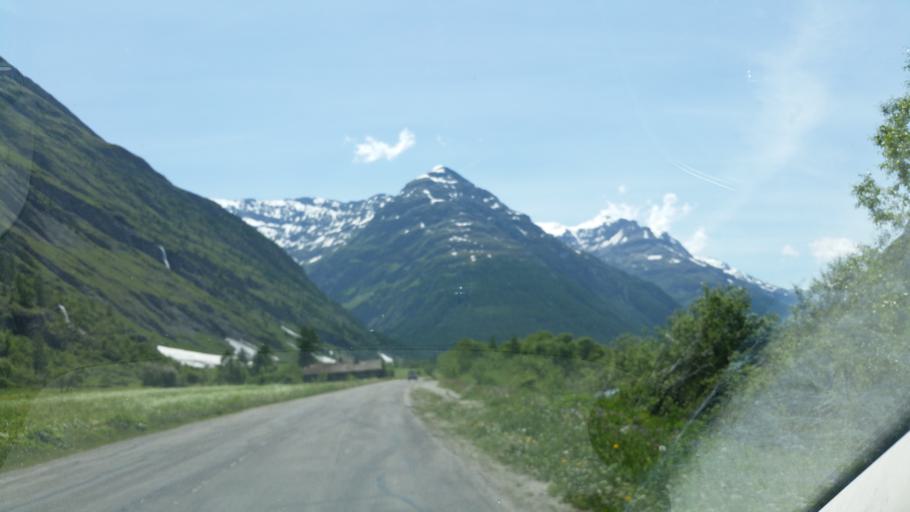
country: FR
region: Rhone-Alpes
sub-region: Departement de la Savoie
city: Val-d'Isere
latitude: 45.3466
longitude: 7.0296
